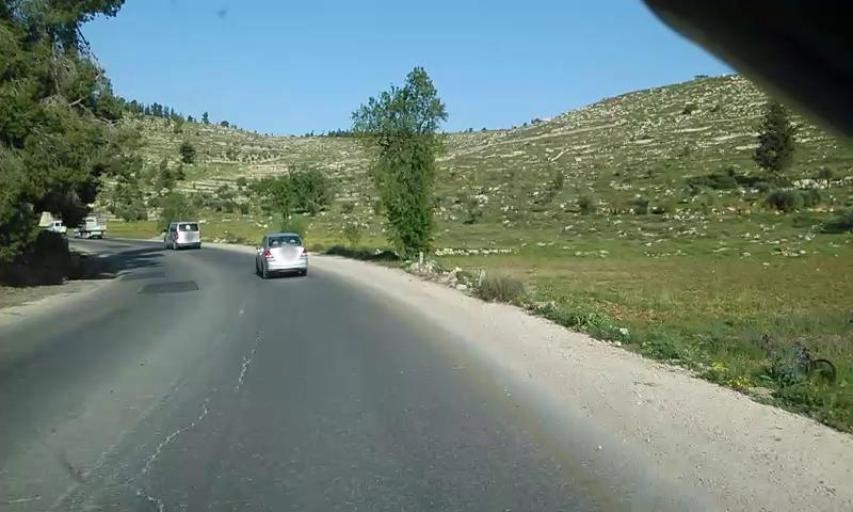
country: PS
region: West Bank
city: Ar Rihiyah
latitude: 31.4881
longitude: 35.0654
